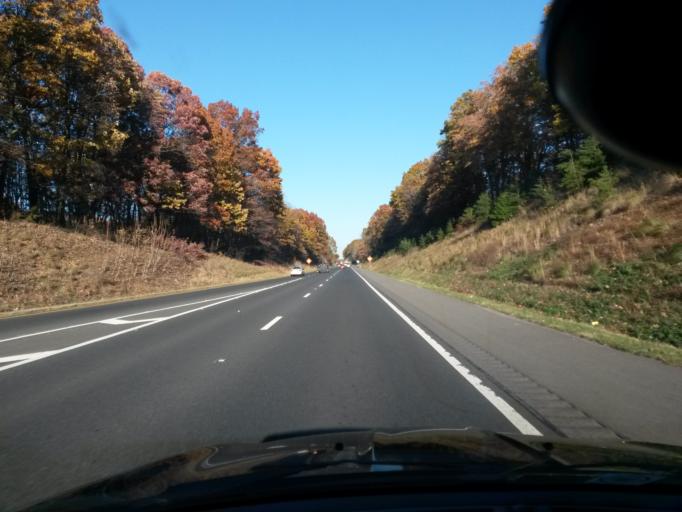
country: US
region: Virginia
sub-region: City of Lynchburg
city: West Lynchburg
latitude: 37.3627
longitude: -79.1628
